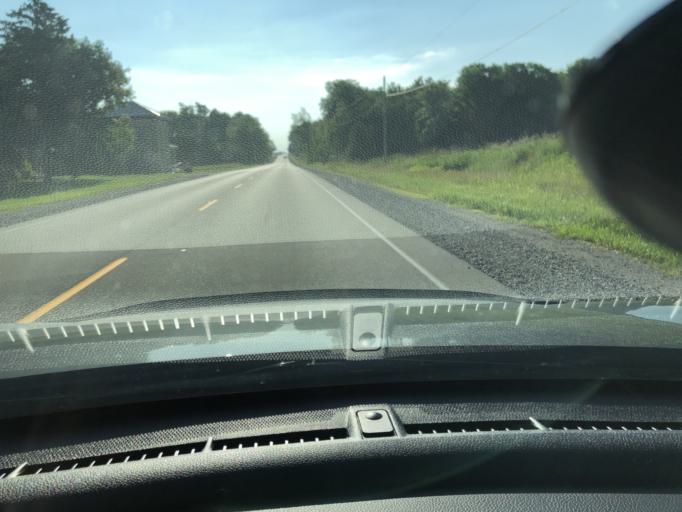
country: CA
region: Ontario
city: Stratford
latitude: 43.4246
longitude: -80.7972
